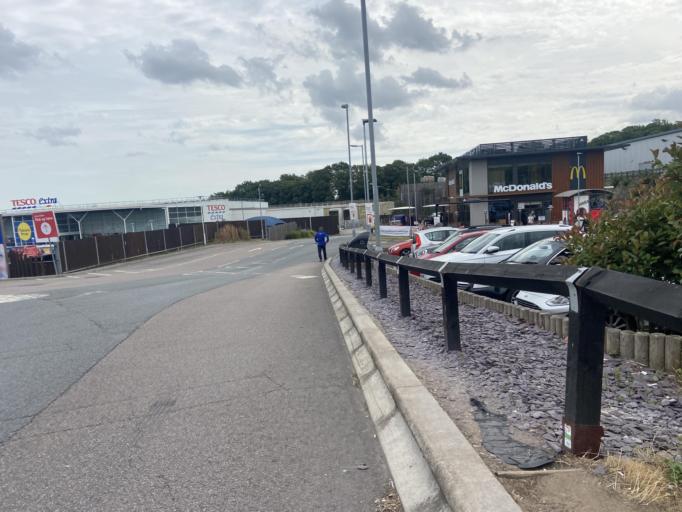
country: GB
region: England
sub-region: Kent
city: Rainham
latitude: 51.3668
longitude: 0.5809
